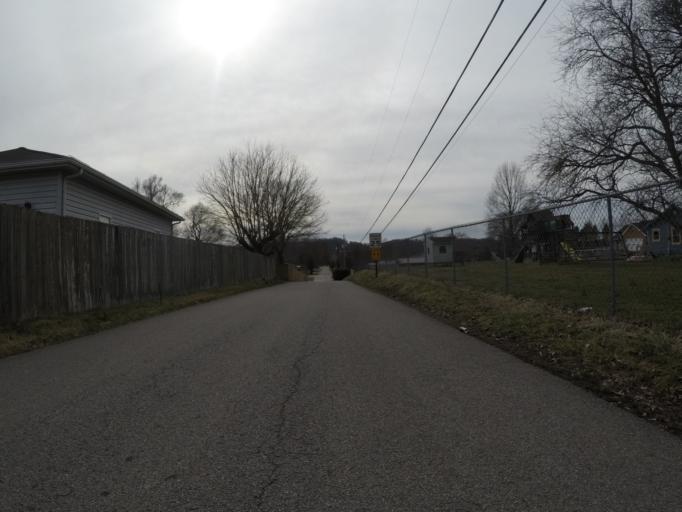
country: US
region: West Virginia
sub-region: Cabell County
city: Pea Ridge
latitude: 38.4537
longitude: -82.3412
